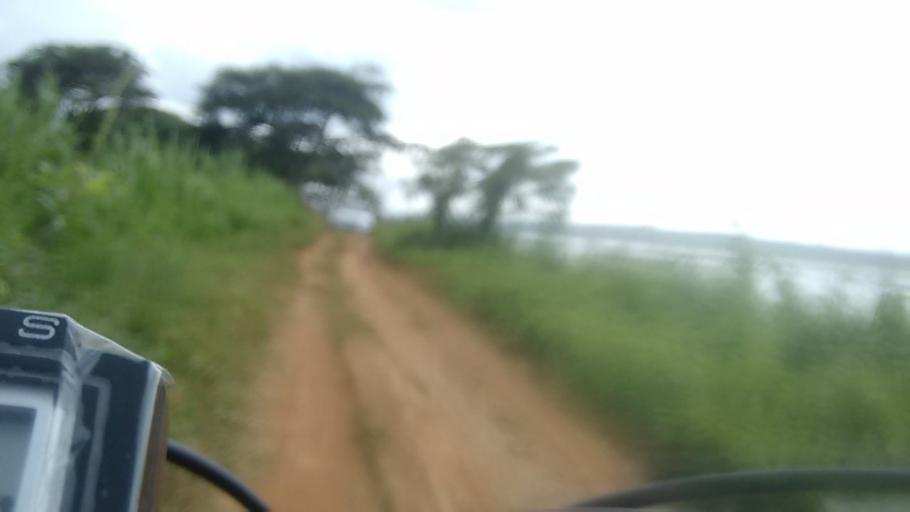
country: IN
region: Kerala
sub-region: Thrissur District
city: Trichur
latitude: 10.5309
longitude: 76.1564
